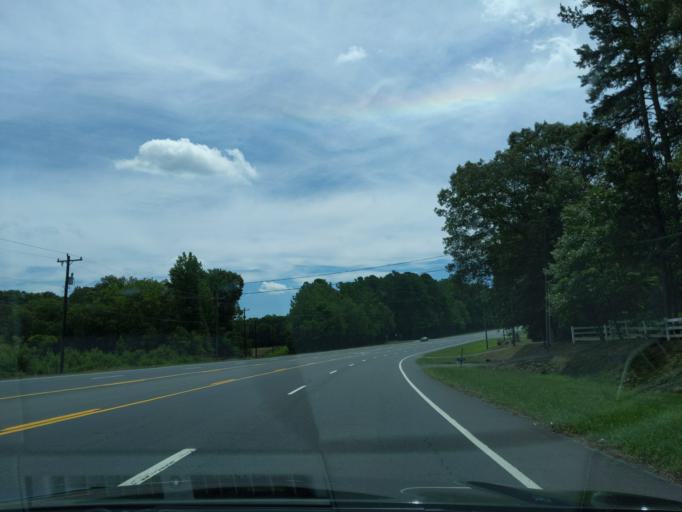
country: US
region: North Carolina
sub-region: Stanly County
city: Albemarle
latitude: 35.4588
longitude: -80.2406
